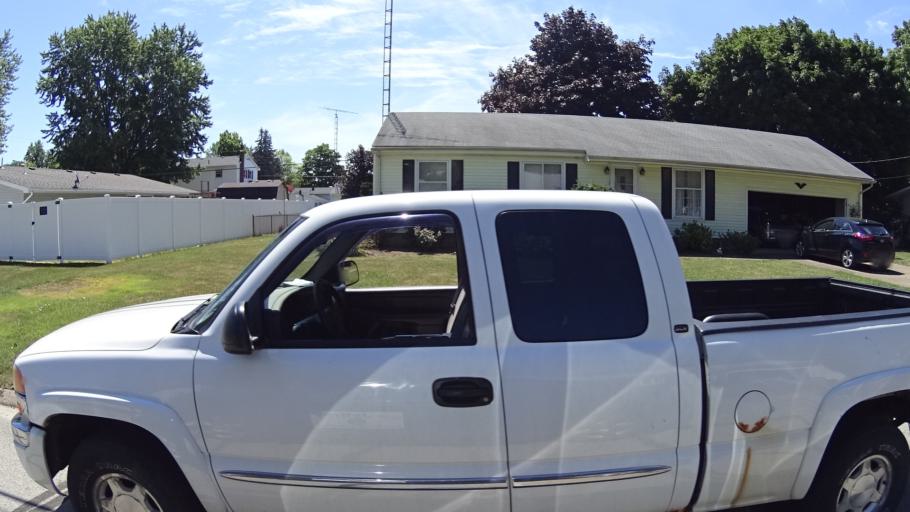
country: US
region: Ohio
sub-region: Erie County
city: Sandusky
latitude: 41.4129
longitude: -82.6902
